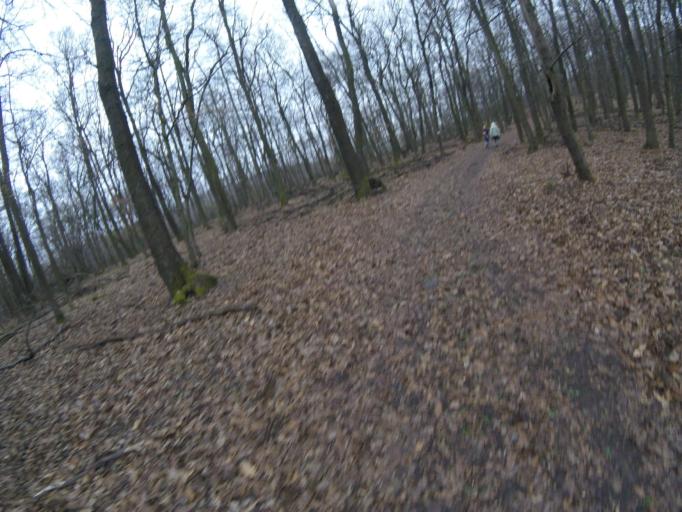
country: HU
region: Pest
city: Szob
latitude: 47.8073
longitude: 18.8262
